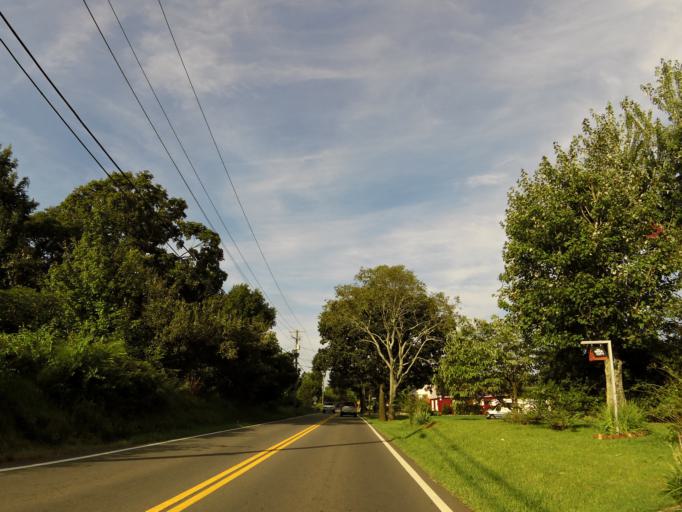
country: US
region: Tennessee
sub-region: Sevier County
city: Seymour
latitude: 35.8688
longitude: -83.7620
